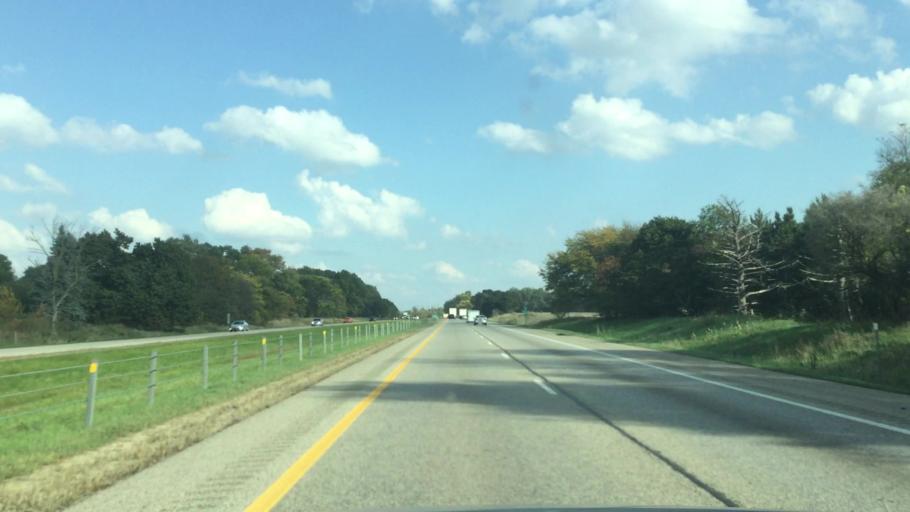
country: US
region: Michigan
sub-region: Calhoun County
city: Lakeview
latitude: 42.2674
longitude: -85.2686
